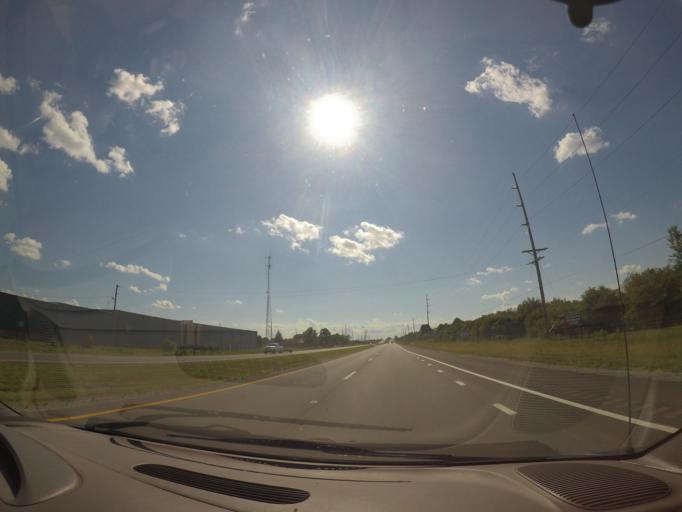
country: US
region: Ohio
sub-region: Sandusky County
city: Stony Prairie
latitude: 41.3685
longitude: -83.1406
